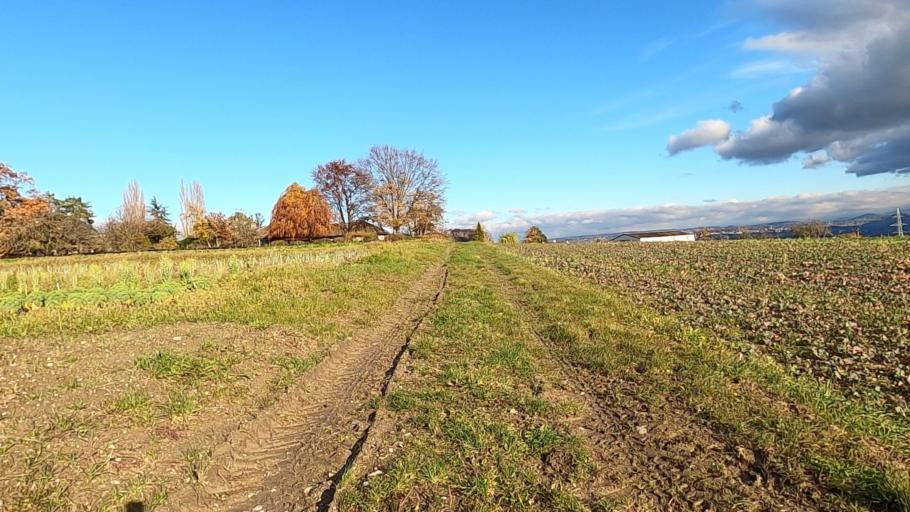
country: CH
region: Vaud
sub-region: Morges District
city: Saint-Prex
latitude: 46.5137
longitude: 6.4521
